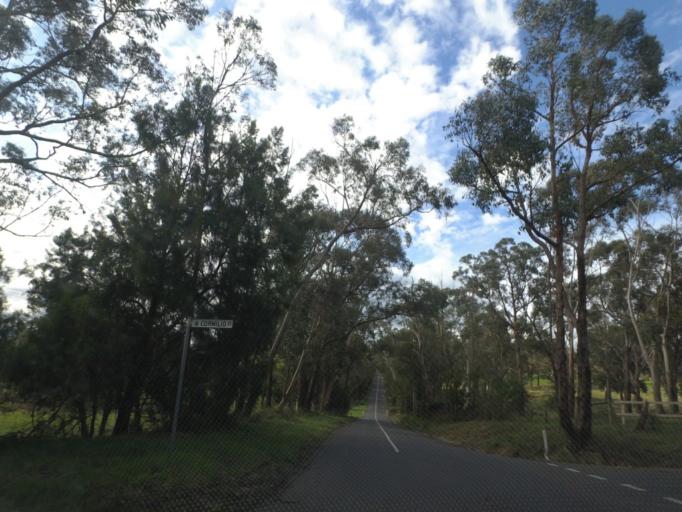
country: AU
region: Victoria
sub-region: Yarra Ranges
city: Mount Evelyn
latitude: -37.7566
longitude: 145.4100
